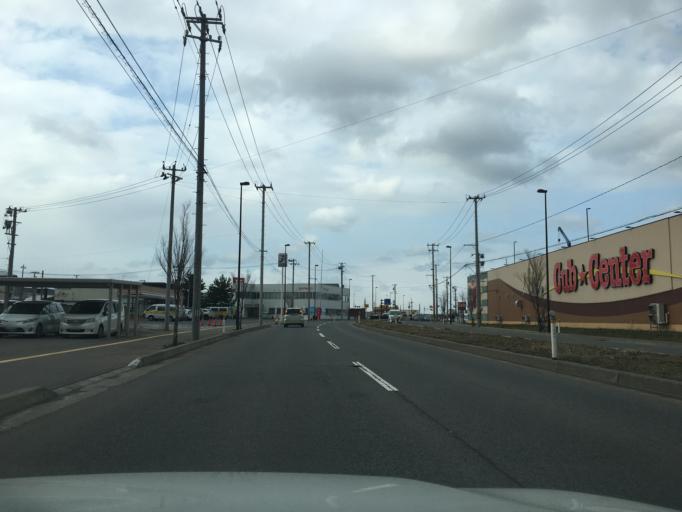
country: JP
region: Aomori
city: Aomori Shi
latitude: 40.8301
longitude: 140.7019
